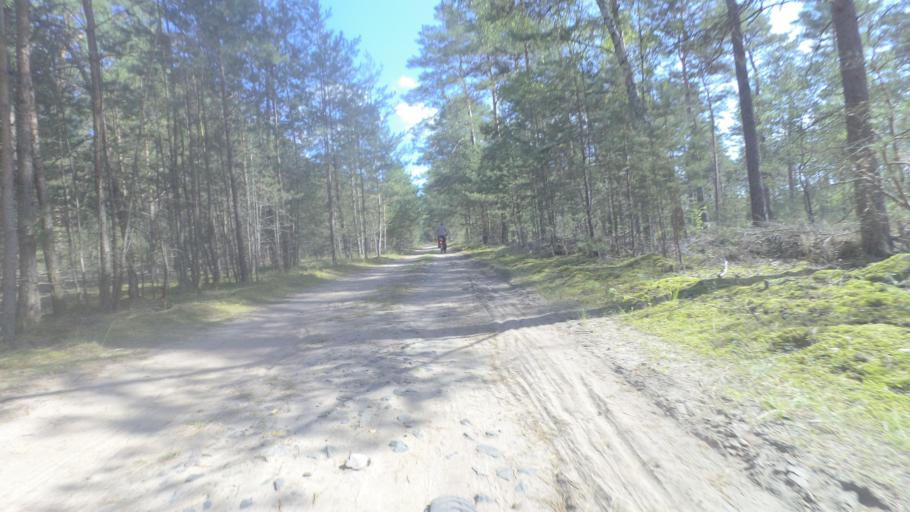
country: DE
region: Brandenburg
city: Halbe
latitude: 52.1494
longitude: 13.7077
